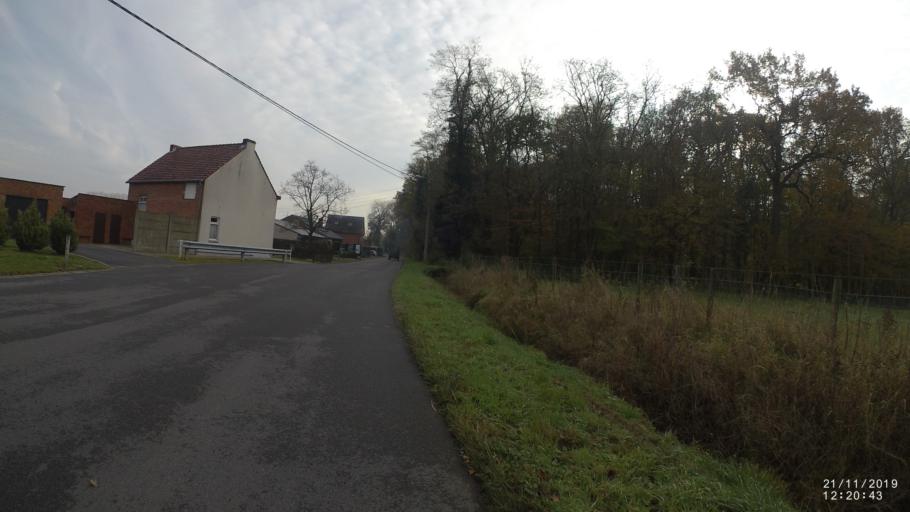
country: BE
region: Flanders
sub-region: Provincie Limburg
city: Alken
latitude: 50.8600
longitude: 5.2537
